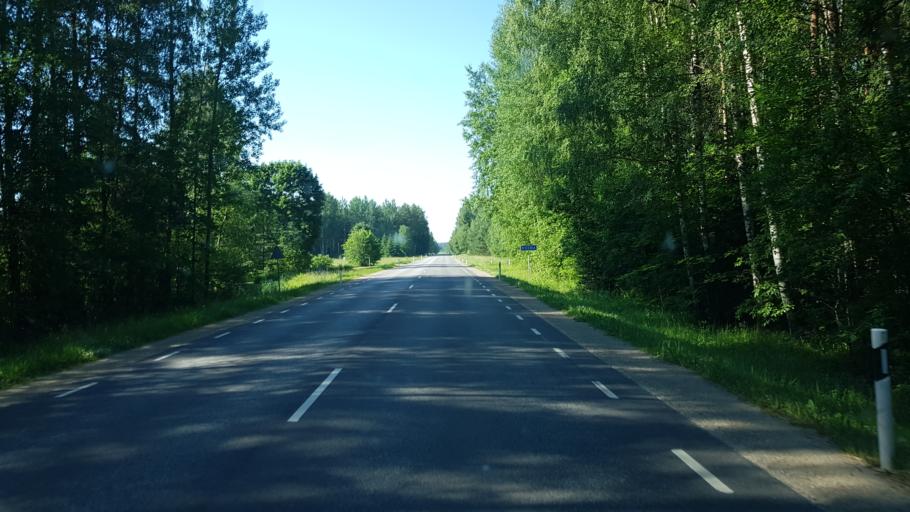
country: EE
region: Polvamaa
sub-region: Polva linn
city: Polva
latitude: 58.0598
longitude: 27.0804
